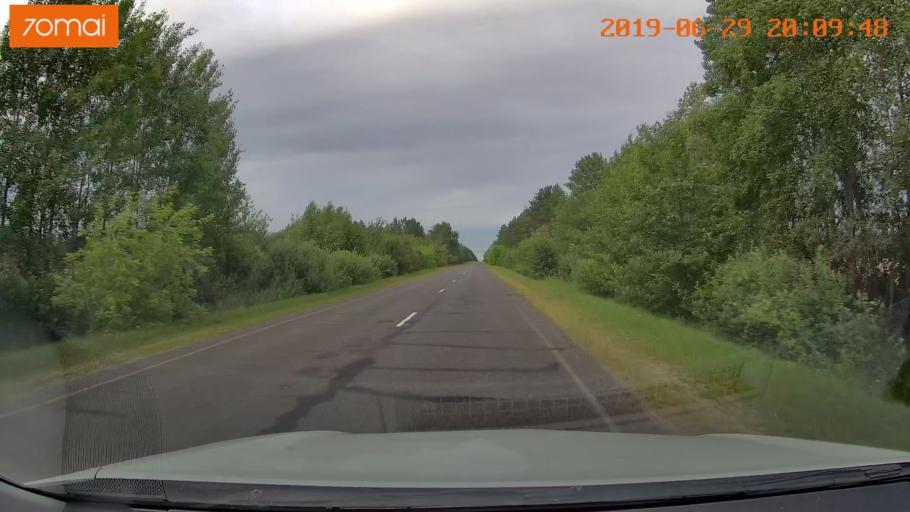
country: BY
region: Brest
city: Lahishyn
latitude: 52.3502
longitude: 26.0792
